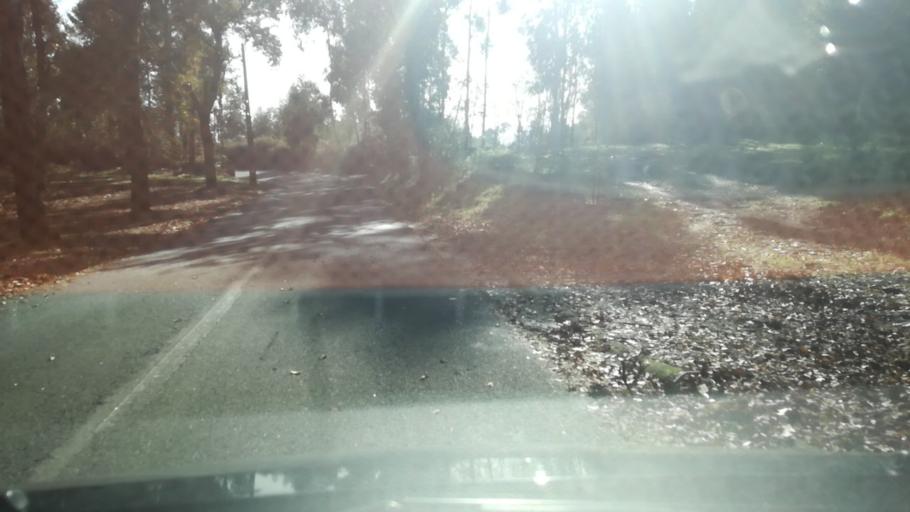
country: PT
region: Braga
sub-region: Braga
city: Braga
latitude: 41.5377
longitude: -8.3669
